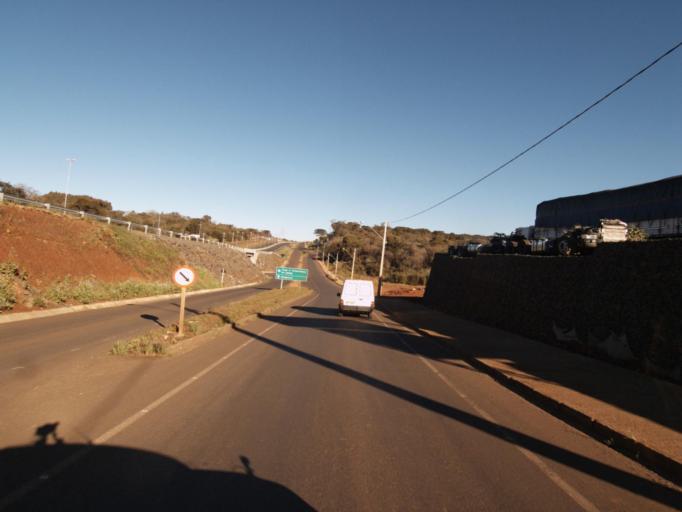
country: BR
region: Santa Catarina
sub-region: Chapeco
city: Chapeco
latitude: -27.0144
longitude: -52.6385
